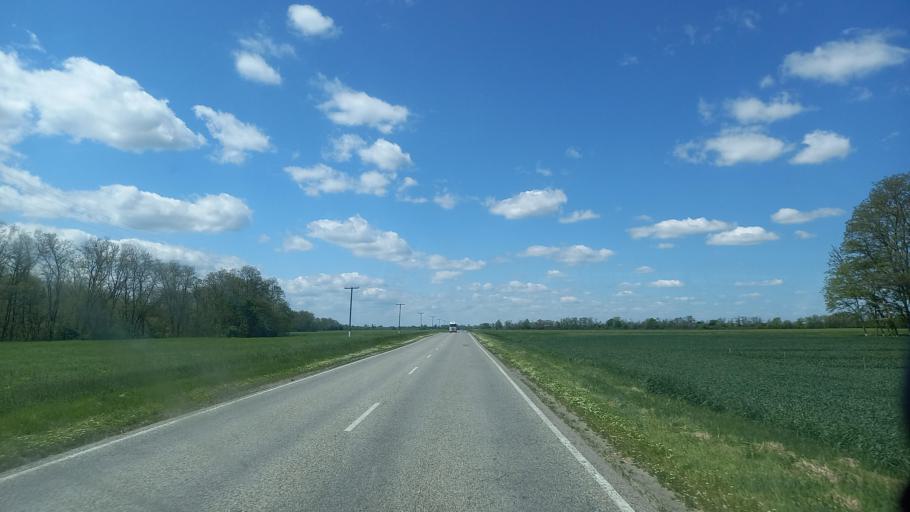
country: RU
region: Krasnodarskiy
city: Kazanskaya
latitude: 45.3579
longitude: 40.3678
